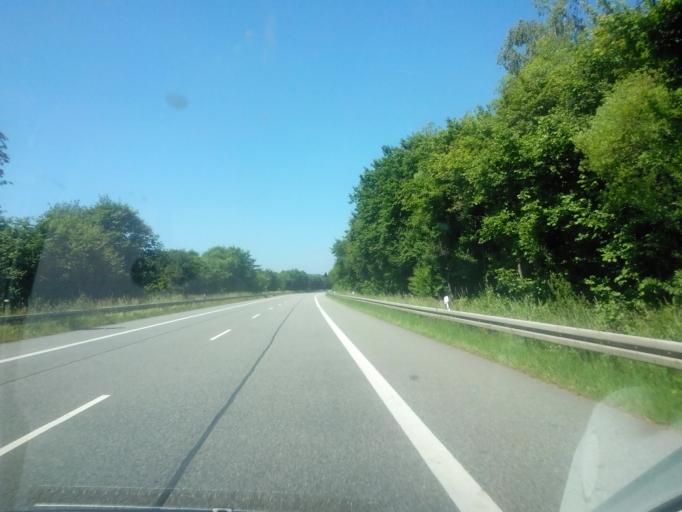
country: DE
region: Saarland
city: Losheim
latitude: 49.5118
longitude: 6.7688
